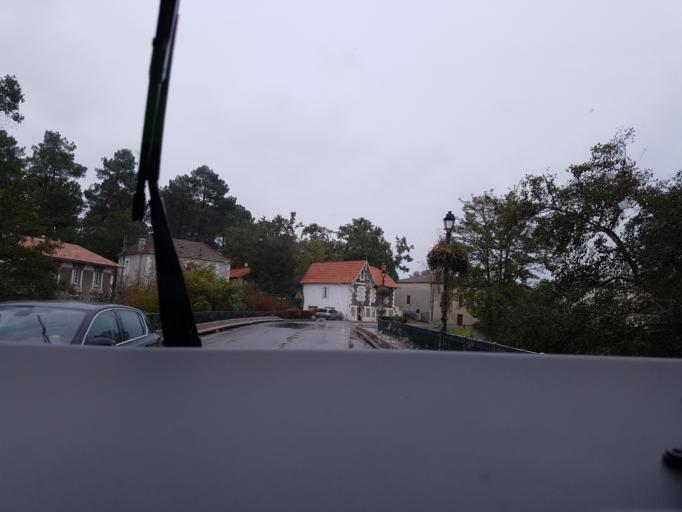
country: FR
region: Aquitaine
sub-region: Departement de la Gironde
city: Saint-Symphorien
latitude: 44.3226
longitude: -0.5851
